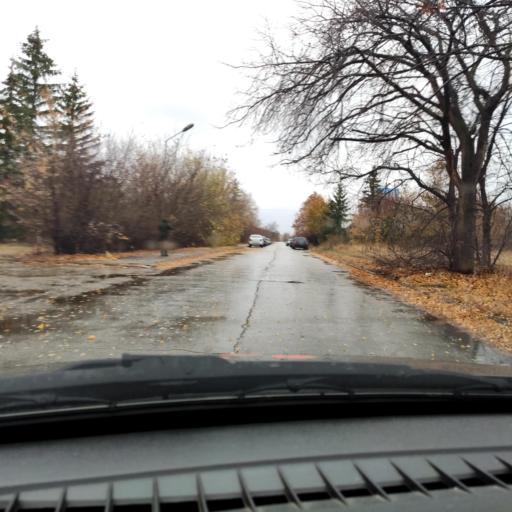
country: RU
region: Samara
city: Tol'yatti
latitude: 53.5531
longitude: 49.2777
